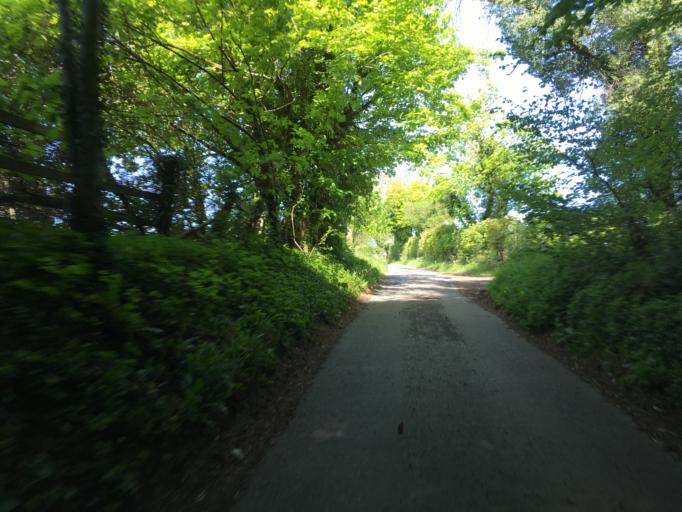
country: GB
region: England
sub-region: Gloucestershire
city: Brimscombe
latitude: 51.7255
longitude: -2.1853
